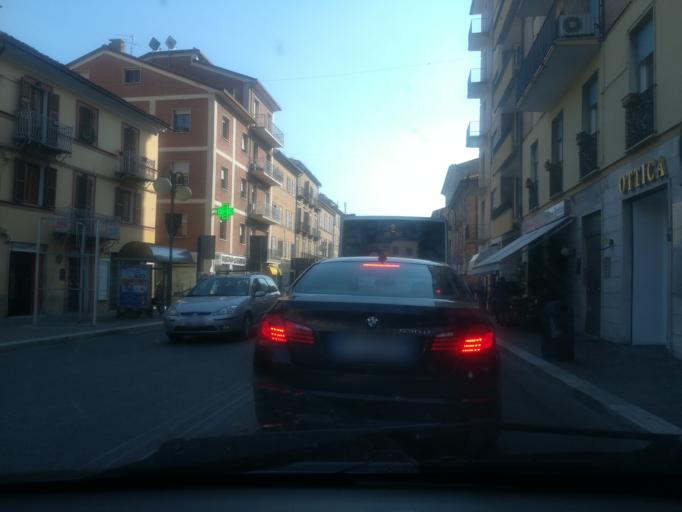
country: IT
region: The Marches
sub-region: Provincia di Macerata
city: Macerata
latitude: 43.2982
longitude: 13.4556
